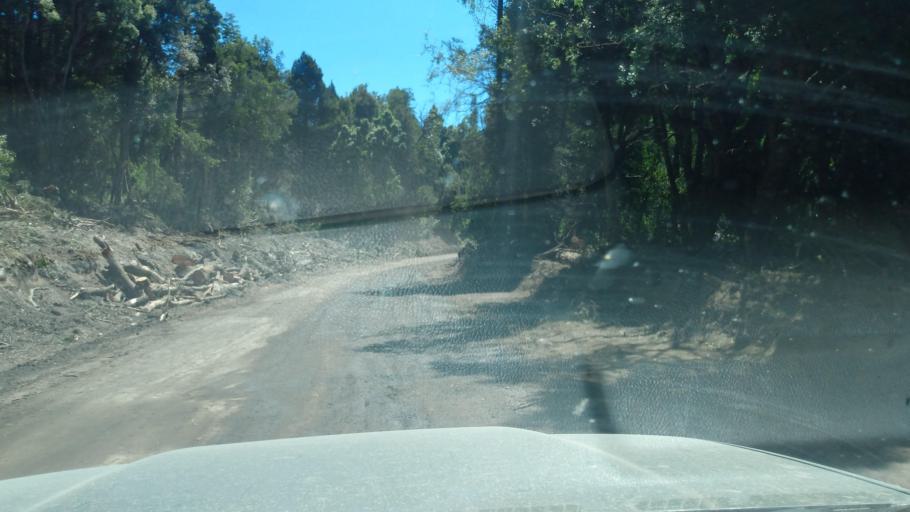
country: AR
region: Neuquen
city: Villa La Angostura
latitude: -40.6244
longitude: -71.5018
